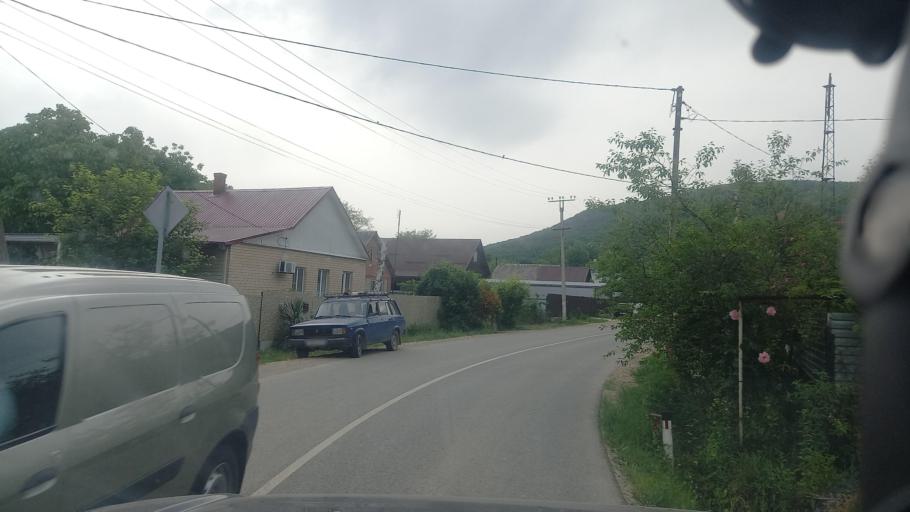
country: RU
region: Krasnodarskiy
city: Goryachiy Klyuch
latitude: 44.6044
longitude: 39.0027
